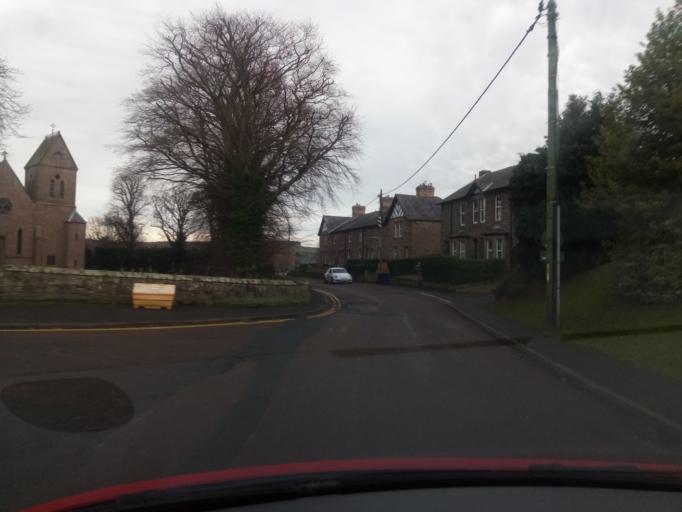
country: GB
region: England
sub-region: Northumberland
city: Wooler
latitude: 55.5478
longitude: -2.0200
